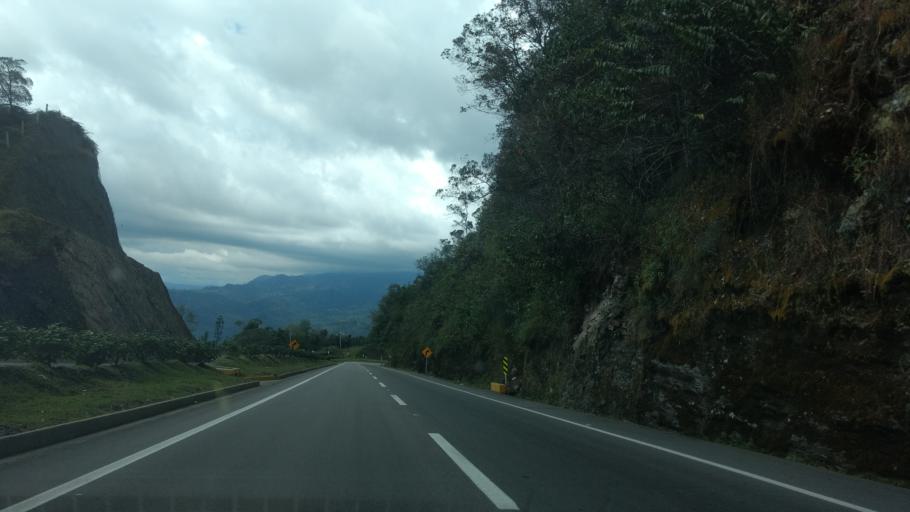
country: CO
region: Cundinamarca
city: San Francisco
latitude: 4.9461
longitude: -74.3053
